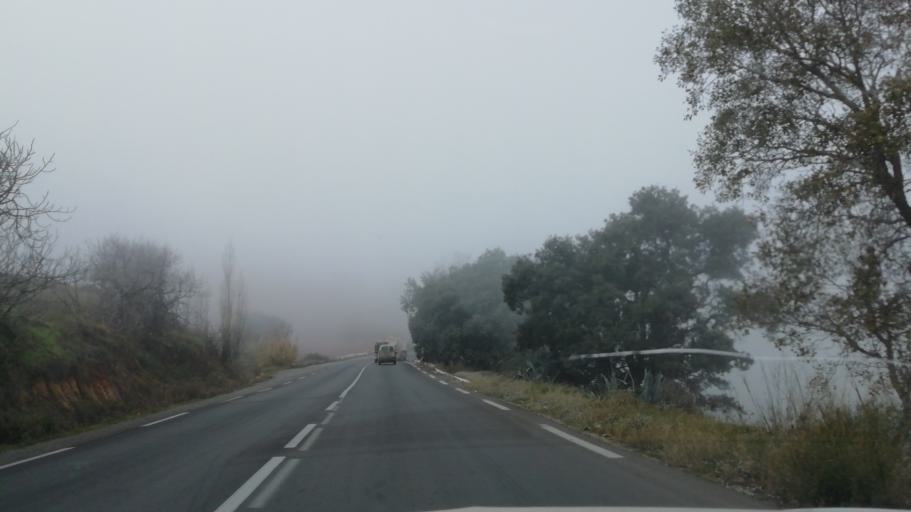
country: DZ
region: Mascara
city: Mascara
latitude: 35.5273
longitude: 0.3352
